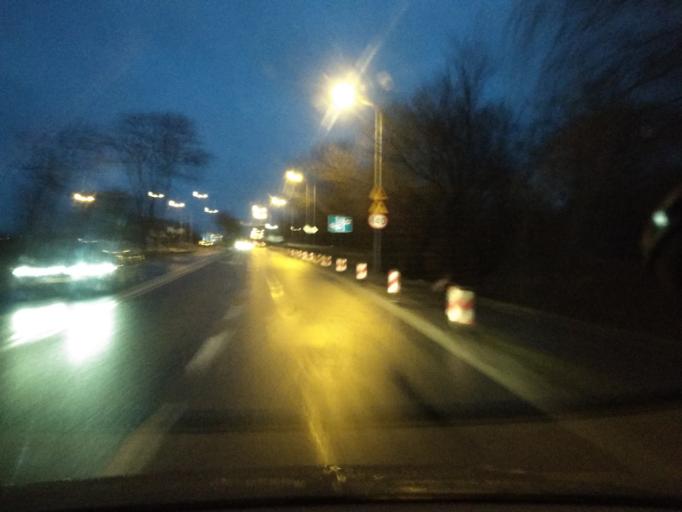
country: PL
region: Lower Silesian Voivodeship
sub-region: Powiat wroclawski
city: Smolec
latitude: 51.1425
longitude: 16.9016
